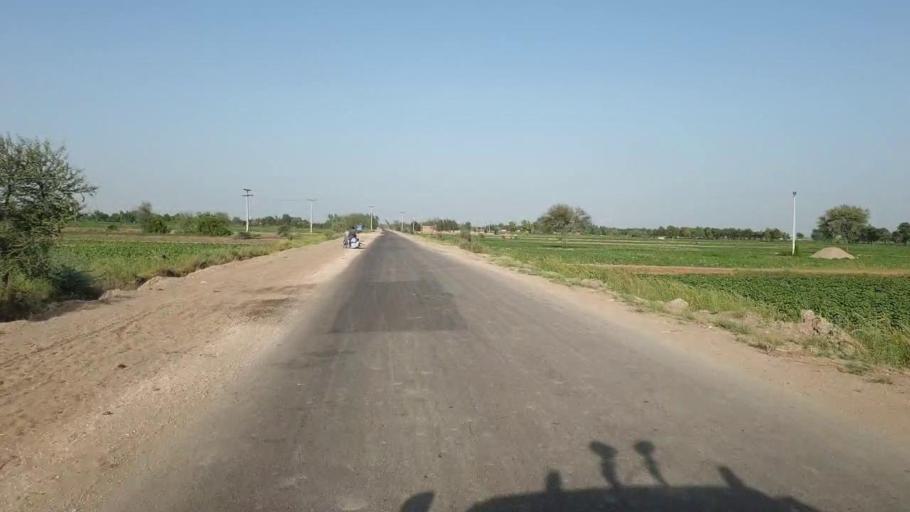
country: PK
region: Sindh
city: Jam Sahib
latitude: 26.3489
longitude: 68.5467
